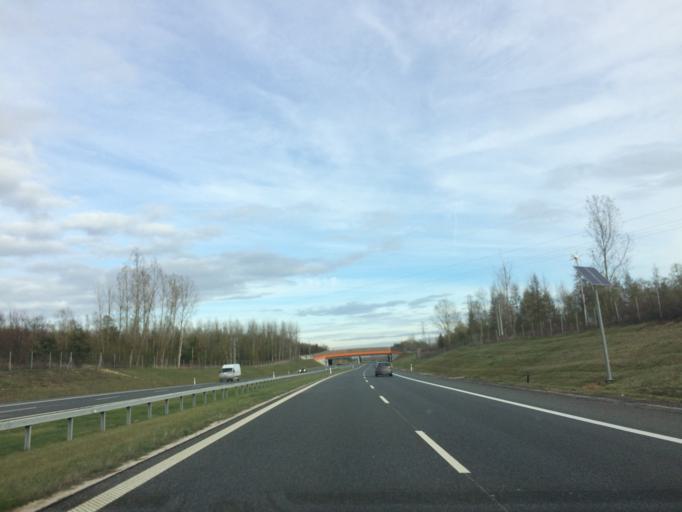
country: PL
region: Lower Silesian Voivodeship
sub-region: Powiat legnicki
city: Milkowice
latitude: 51.1931
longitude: 16.0948
